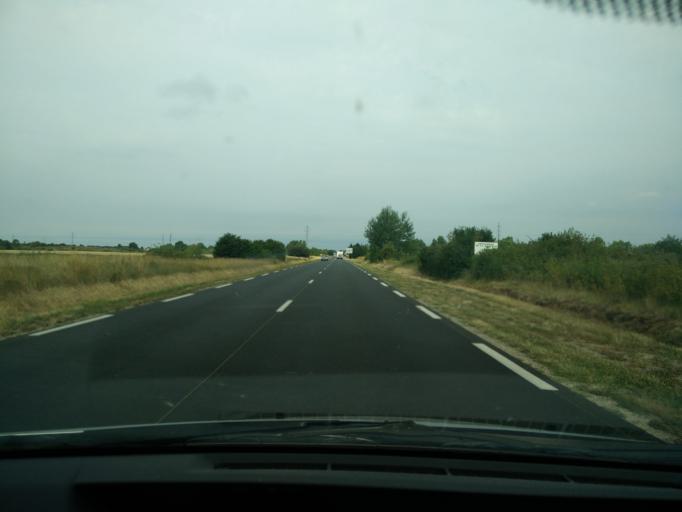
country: FR
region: Pays de la Loire
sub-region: Departement de Maine-et-Loire
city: Doue-la-Fontaine
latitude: 47.1796
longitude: -0.2403
